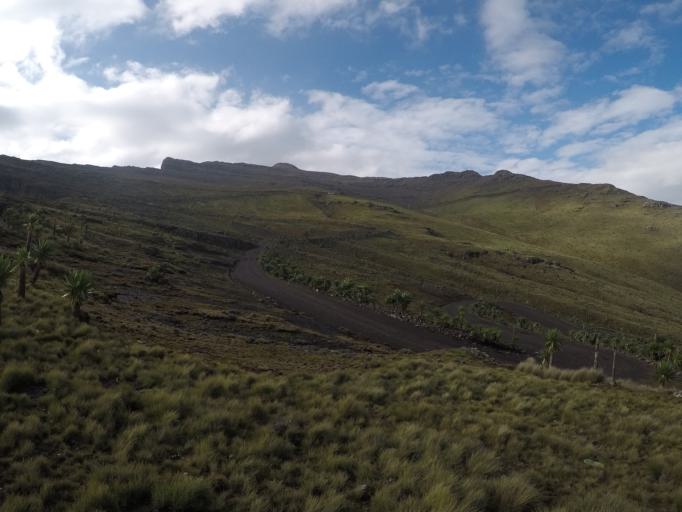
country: ET
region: Amhara
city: Debark'
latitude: 13.2587
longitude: 38.2160
